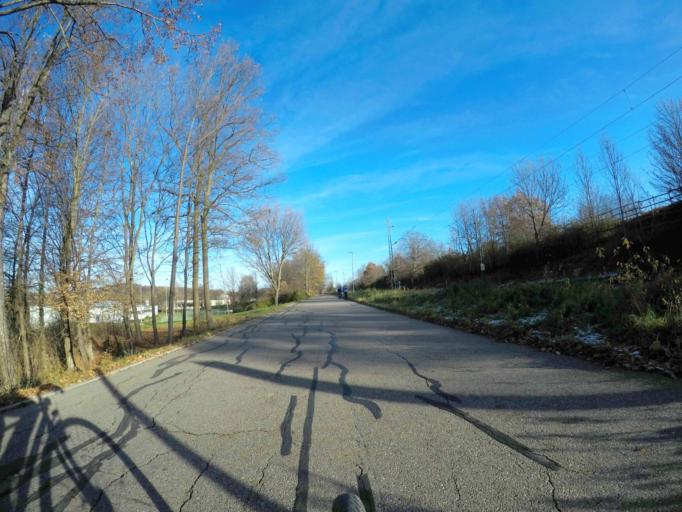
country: DE
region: Baden-Wuerttemberg
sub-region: Tuebingen Region
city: Reutlingen
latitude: 48.5134
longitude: 9.2273
